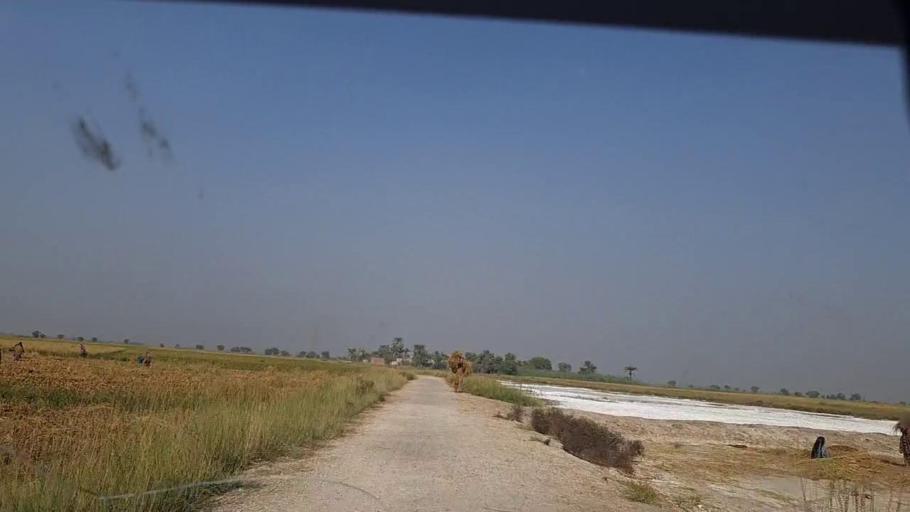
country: PK
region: Sindh
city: Shikarpur
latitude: 28.0924
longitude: 68.5996
